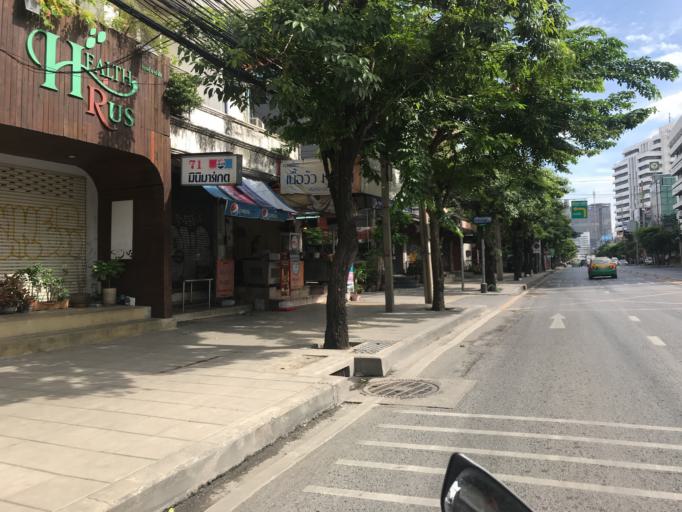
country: TH
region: Bangkok
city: Watthana
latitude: 13.7310
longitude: 100.5966
